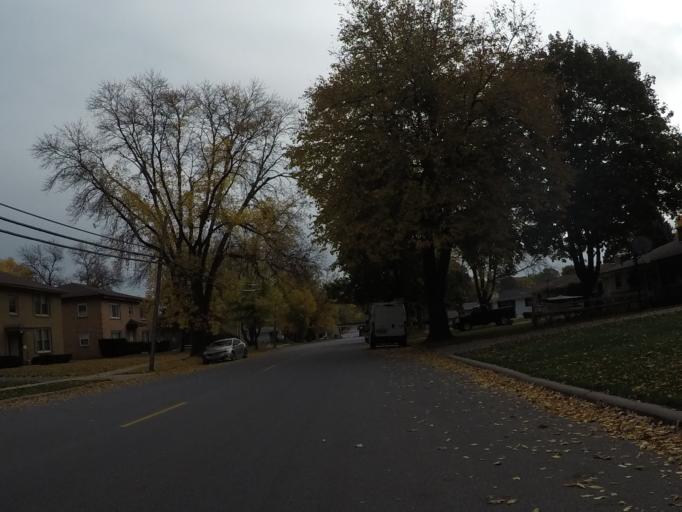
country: US
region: Wisconsin
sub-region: Dane County
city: Maple Bluff
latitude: 43.1338
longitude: -89.3869
